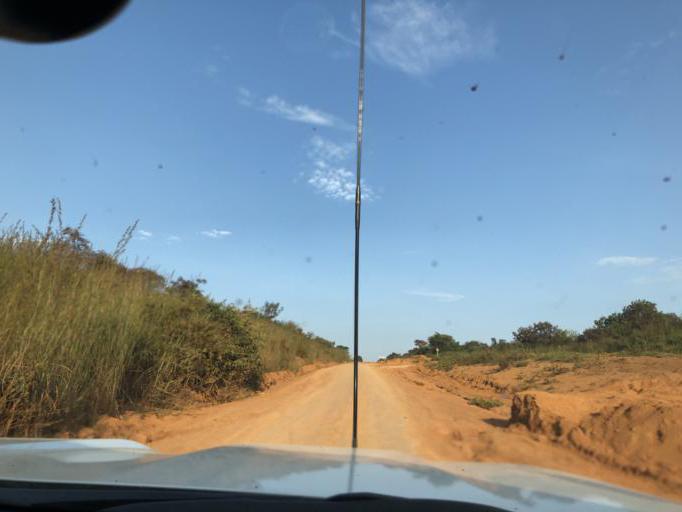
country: CF
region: Nana-Mambere
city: Bouar
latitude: 5.8950
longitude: 15.7615
